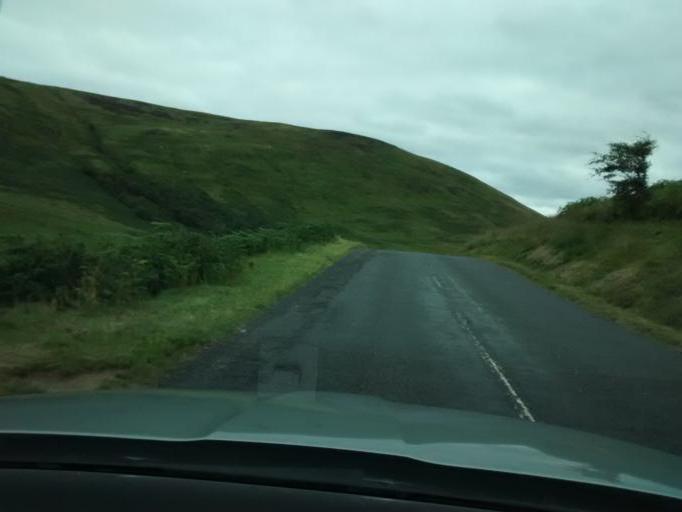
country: GB
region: Scotland
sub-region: North Ayrshire
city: Isle of Arran
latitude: 55.7007
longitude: -5.2603
